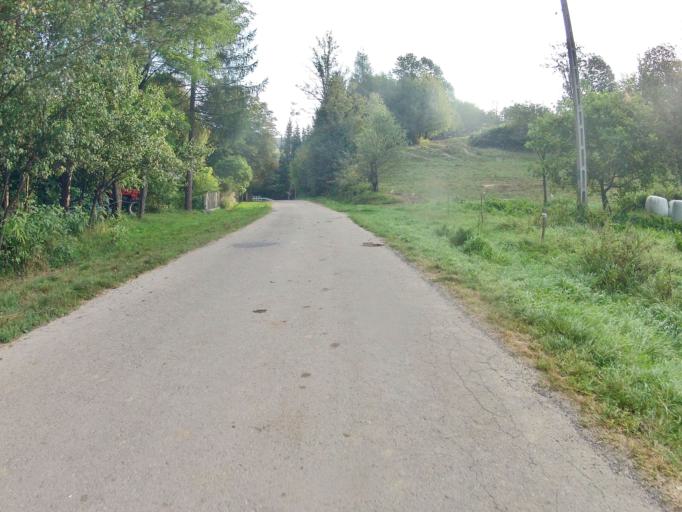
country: PL
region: Subcarpathian Voivodeship
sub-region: Powiat jasielski
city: Krempna
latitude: 49.5402
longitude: 21.5519
